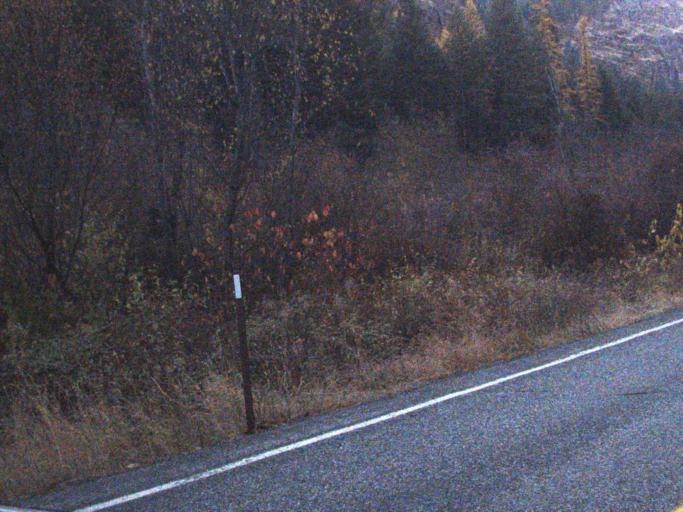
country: US
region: Washington
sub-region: Ferry County
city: Republic
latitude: 48.4960
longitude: -118.7410
